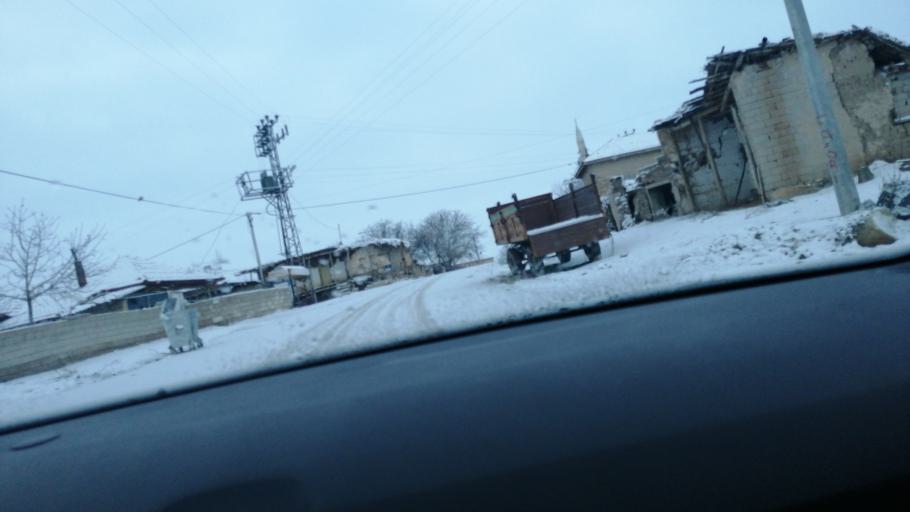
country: TR
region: Aksaray
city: Agacoren
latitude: 38.9349
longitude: 33.9488
